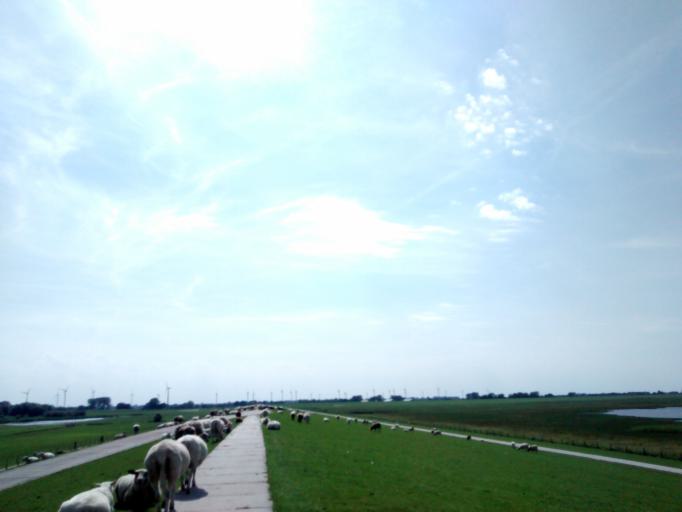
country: DE
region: Lower Saxony
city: Varel
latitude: 53.4455
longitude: 8.1062
